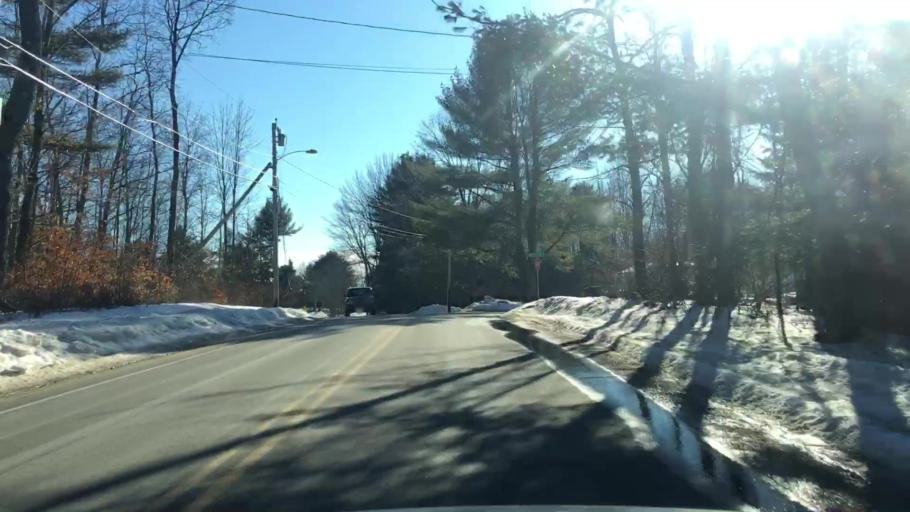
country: US
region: Maine
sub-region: Cumberland County
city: Westbrook
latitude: 43.7364
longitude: -70.3567
